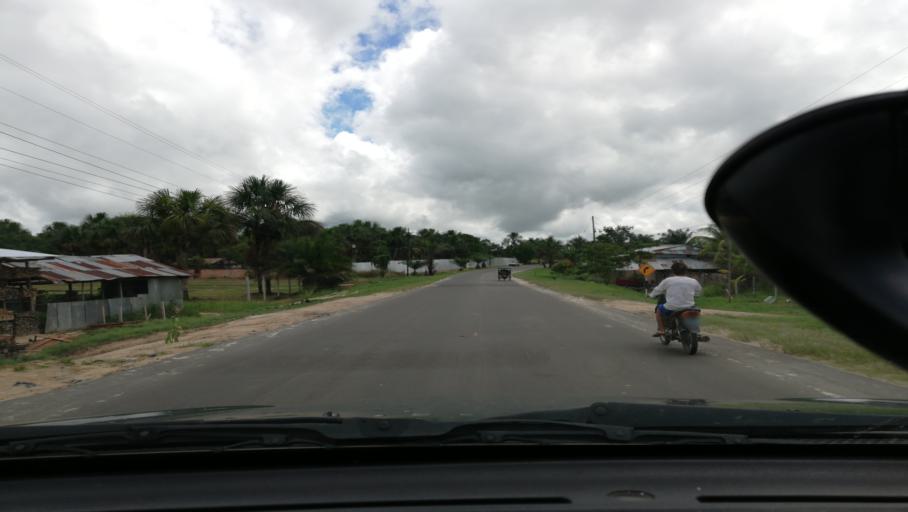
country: PE
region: Loreto
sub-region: Provincia de Maynas
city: Iquitos
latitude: -3.8528
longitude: -73.3381
